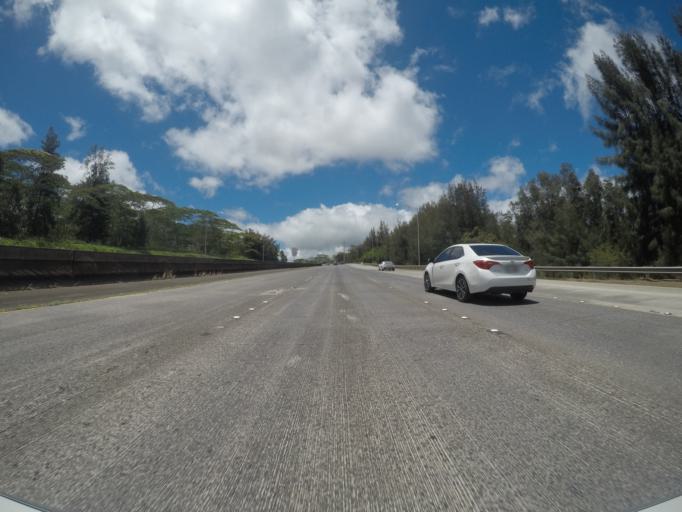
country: US
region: Hawaii
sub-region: Honolulu County
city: Mililani Town
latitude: 21.4441
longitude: -157.9924
